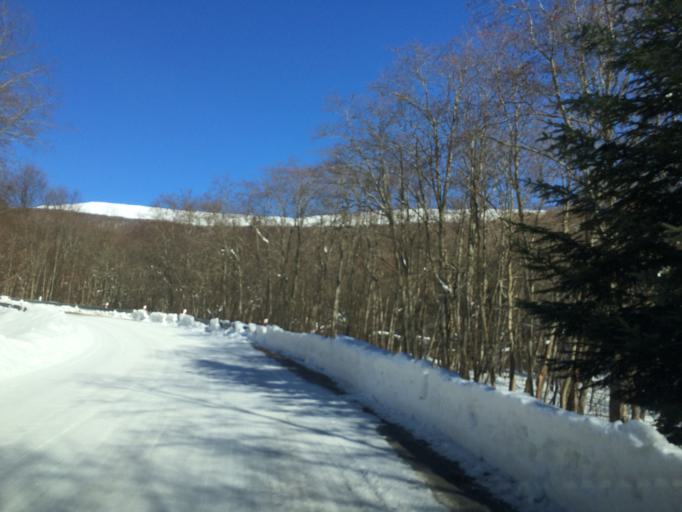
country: PL
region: Subcarpathian Voivodeship
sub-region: Powiat bieszczadzki
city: Lutowiska
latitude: 49.1179
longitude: 22.6103
